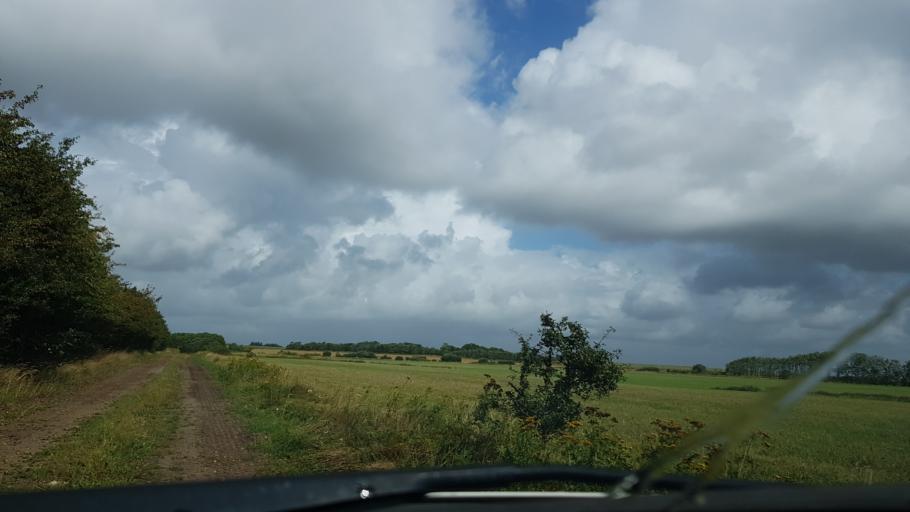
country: DK
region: South Denmark
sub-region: Esbjerg Kommune
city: Ribe
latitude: 55.2523
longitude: 8.7662
